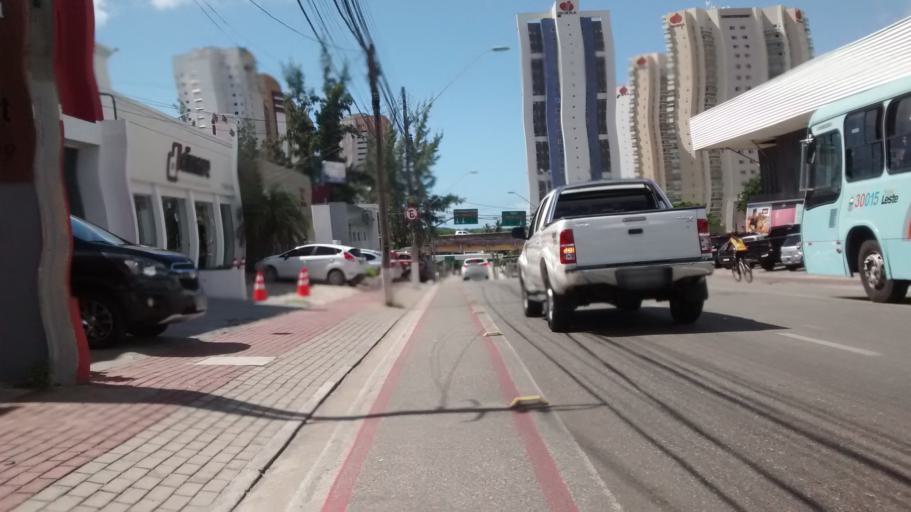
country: BR
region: Ceara
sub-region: Fortaleza
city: Fortaleza
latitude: -3.7480
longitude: -38.4942
